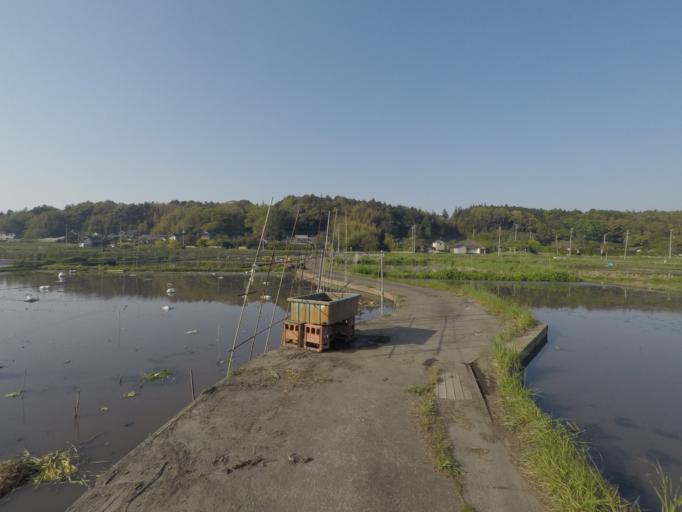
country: JP
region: Ibaraki
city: Ami
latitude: 36.0673
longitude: 140.2816
